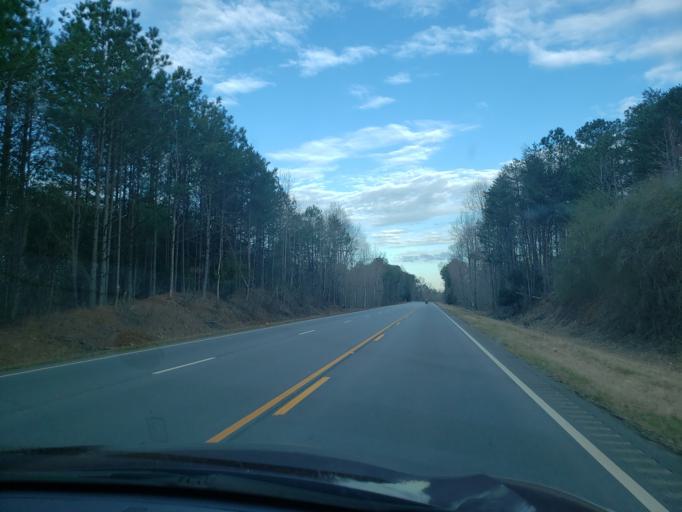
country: US
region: Alabama
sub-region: Randolph County
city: Roanoke
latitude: 33.2238
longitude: -85.4260
